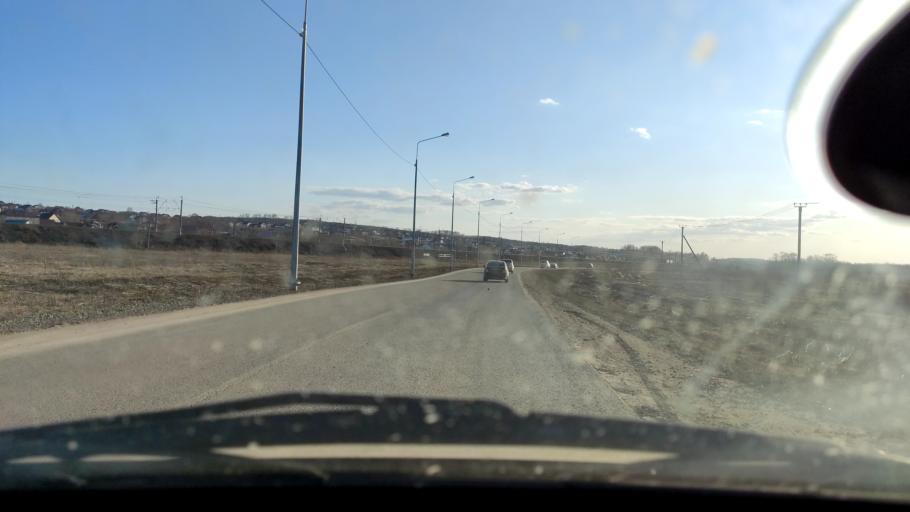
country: RU
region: Bashkortostan
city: Kabakovo
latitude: 54.6425
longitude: 56.0809
